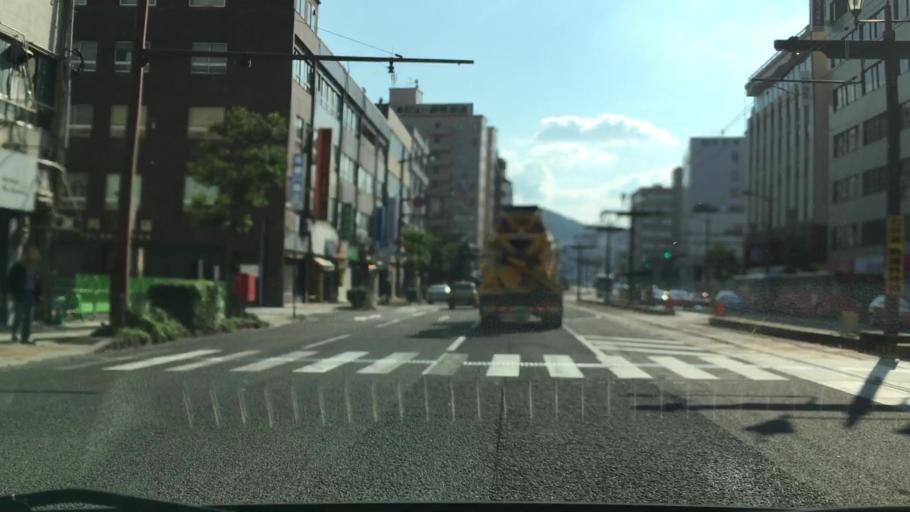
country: JP
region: Nagasaki
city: Nagasaki-shi
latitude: 32.7470
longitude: 129.8724
